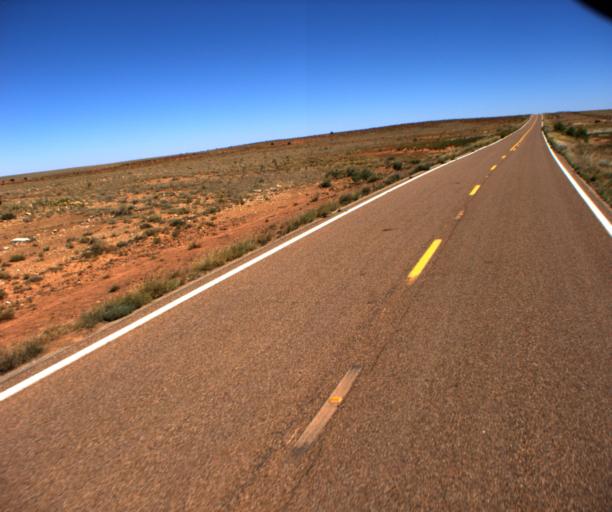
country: US
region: Arizona
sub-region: Navajo County
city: Winslow
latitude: 34.8570
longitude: -110.6634
